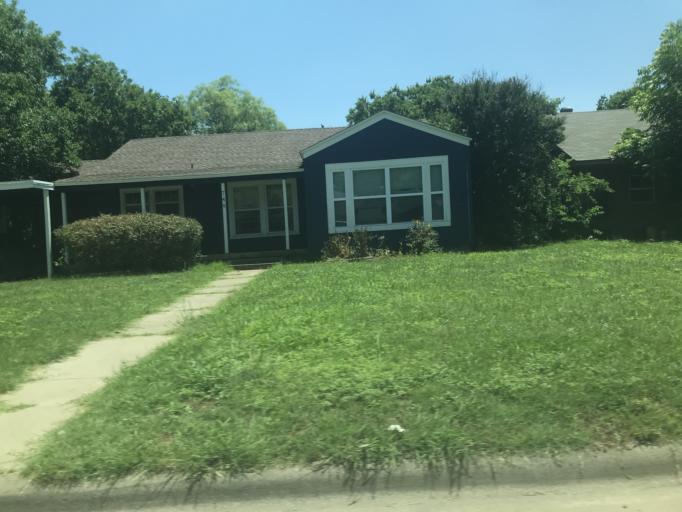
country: US
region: Texas
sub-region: Taylor County
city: Abilene
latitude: 32.4609
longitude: -99.7109
